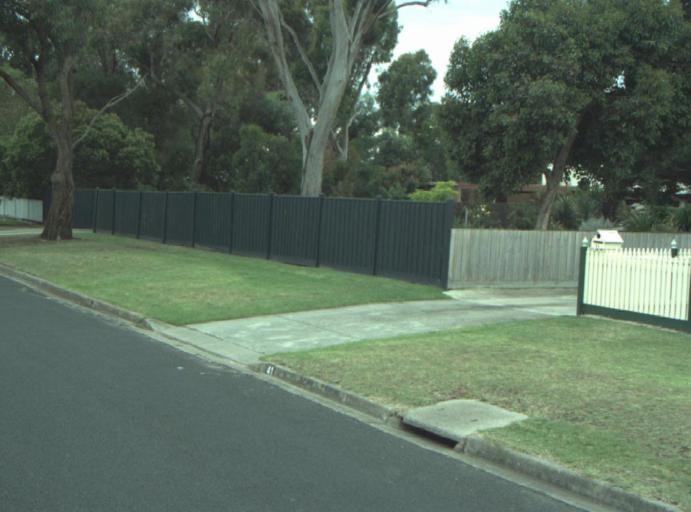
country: AU
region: Victoria
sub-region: Greater Geelong
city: East Geelong
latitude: -38.1653
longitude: 144.4001
